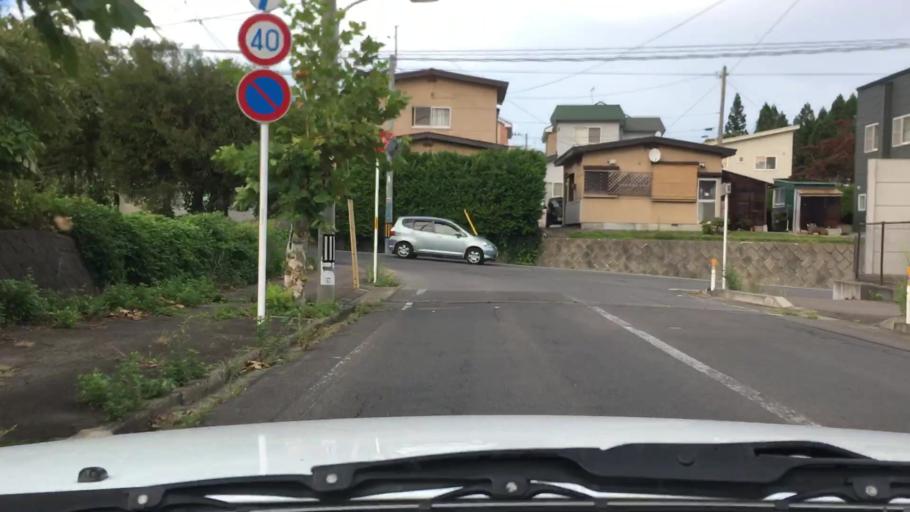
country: JP
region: Aomori
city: Hirosaki
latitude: 40.5777
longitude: 140.4569
